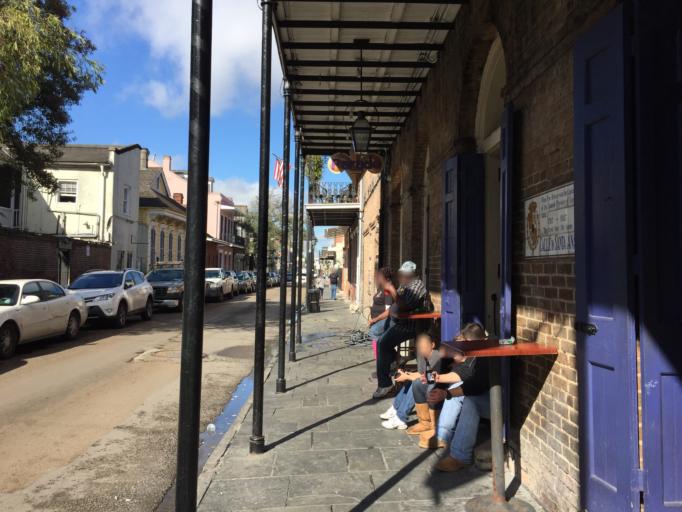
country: US
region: Louisiana
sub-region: Orleans Parish
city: New Orleans
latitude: 29.9595
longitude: -90.0649
